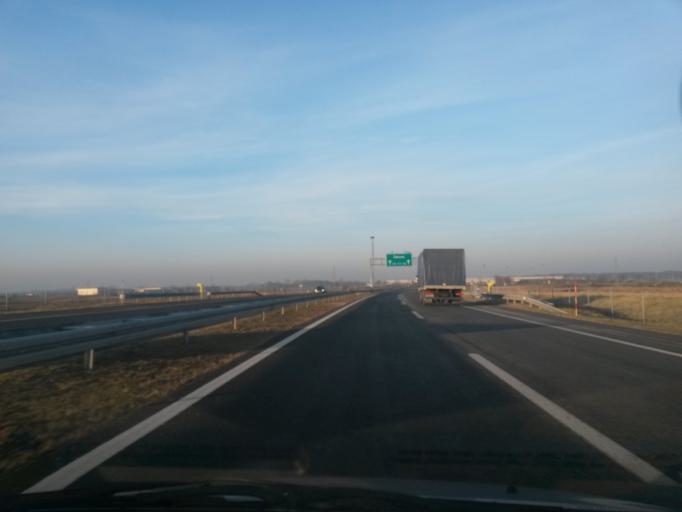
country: HR
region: Medimurska
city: Kursanec
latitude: 46.2554
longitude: 16.3988
